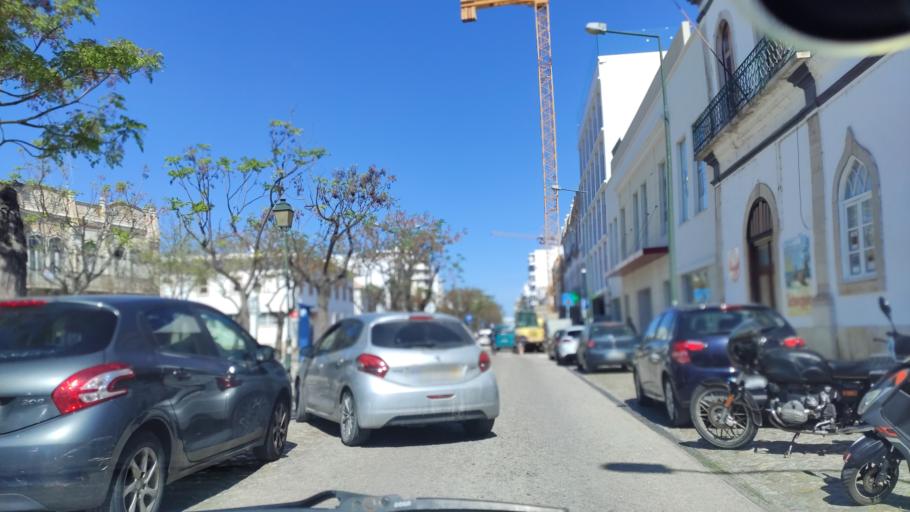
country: PT
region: Faro
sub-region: Olhao
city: Olhao
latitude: 37.0268
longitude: -7.8400
